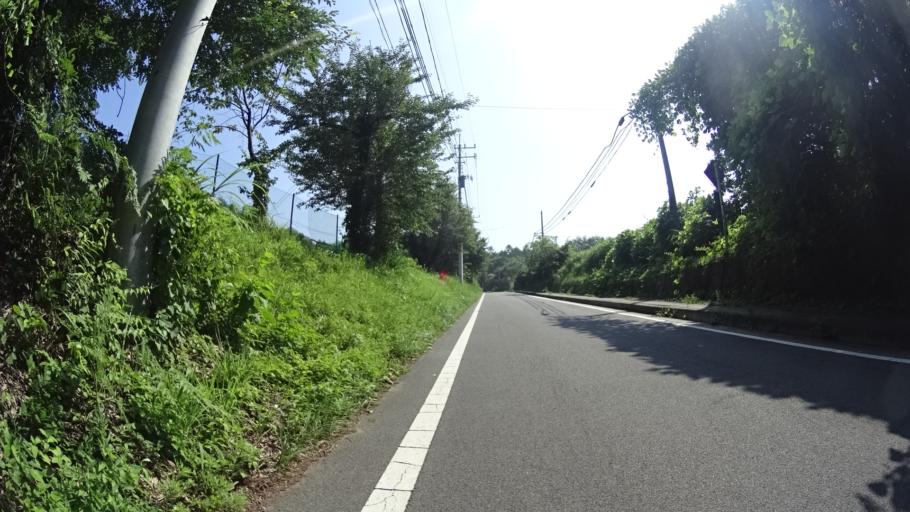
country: JP
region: Yamanashi
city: Nirasaki
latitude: 35.8669
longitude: 138.3291
